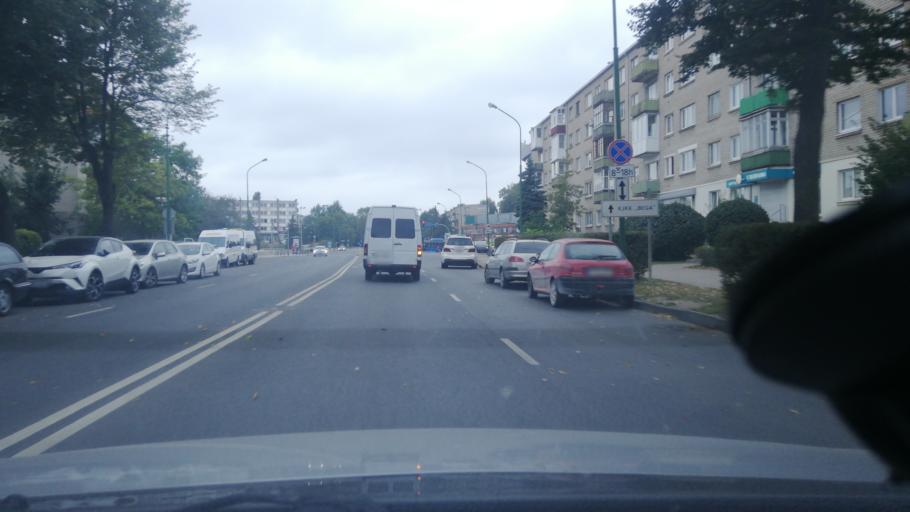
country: LT
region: Klaipedos apskritis
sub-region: Klaipeda
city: Klaipeda
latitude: 55.7034
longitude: 21.1467
